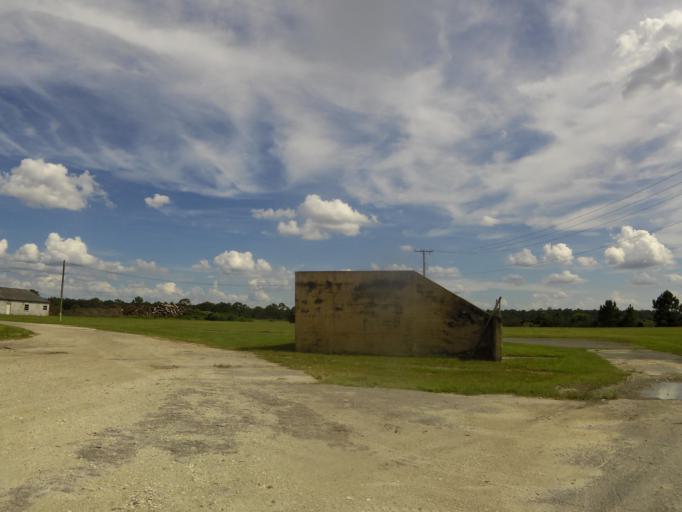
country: US
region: Florida
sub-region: Clay County
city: Green Cove Springs
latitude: 29.9787
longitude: -81.6535
